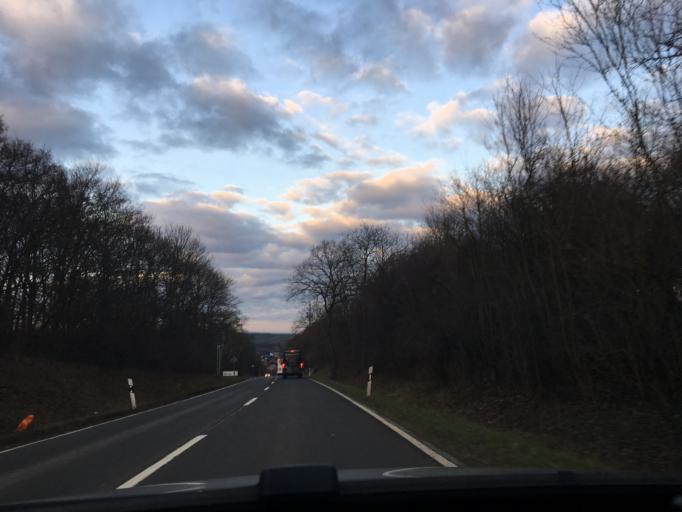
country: DE
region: Rheinland-Pfalz
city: Kettenheim
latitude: 49.7335
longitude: 8.1066
